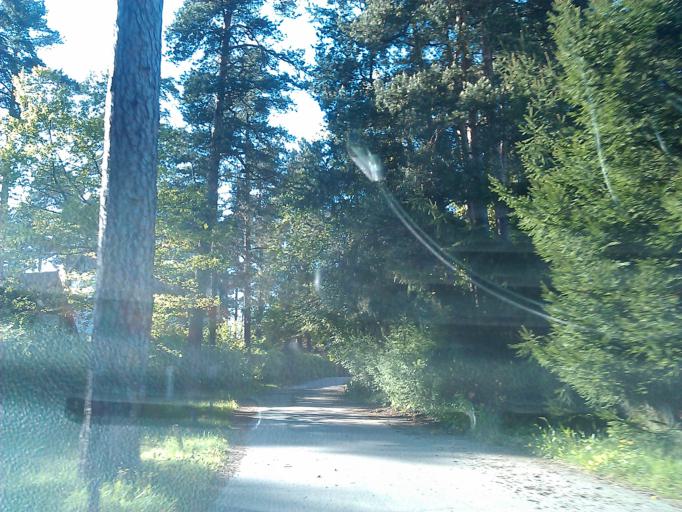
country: LV
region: Riga
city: Bergi
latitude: 57.0152
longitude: 24.2734
